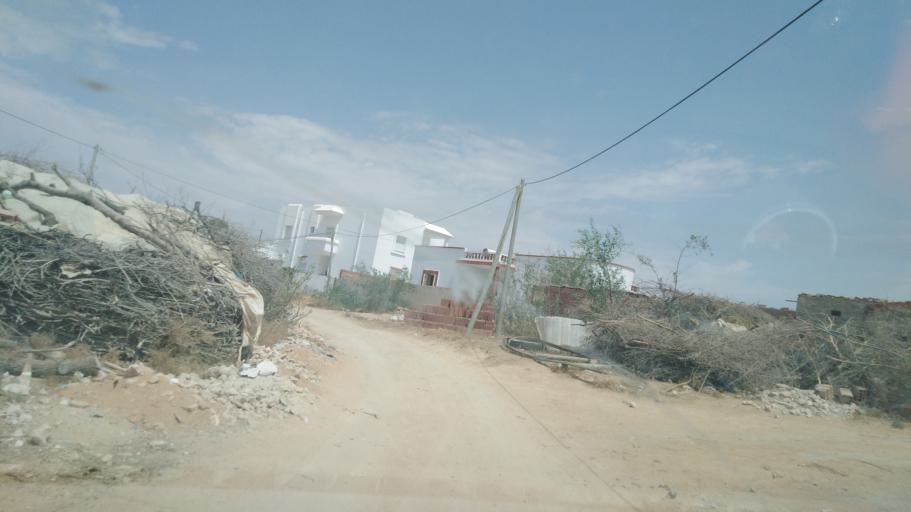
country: TN
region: Safaqis
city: Sfax
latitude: 34.7422
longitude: 10.5611
